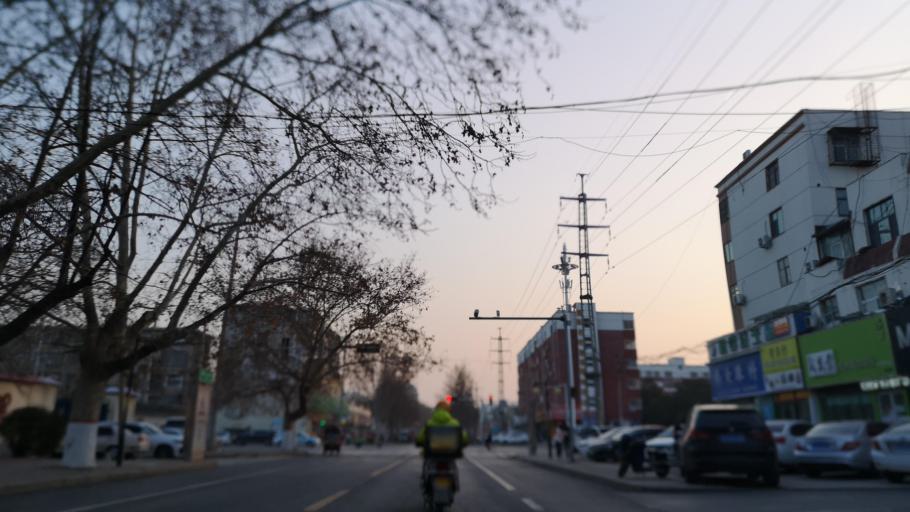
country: CN
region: Henan Sheng
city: Zhongyuanlu
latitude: 35.7689
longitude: 115.0745
